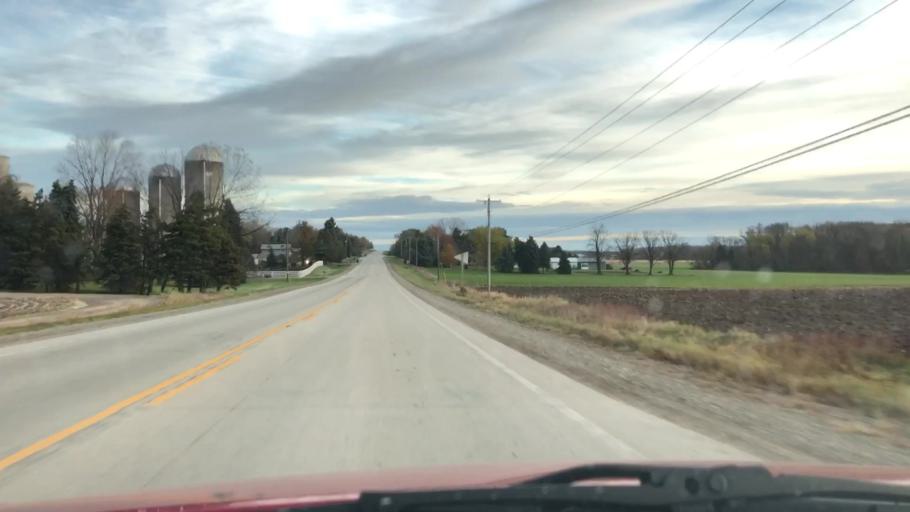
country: US
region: Wisconsin
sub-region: Brown County
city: Oneida
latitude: 44.4250
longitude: -88.2444
